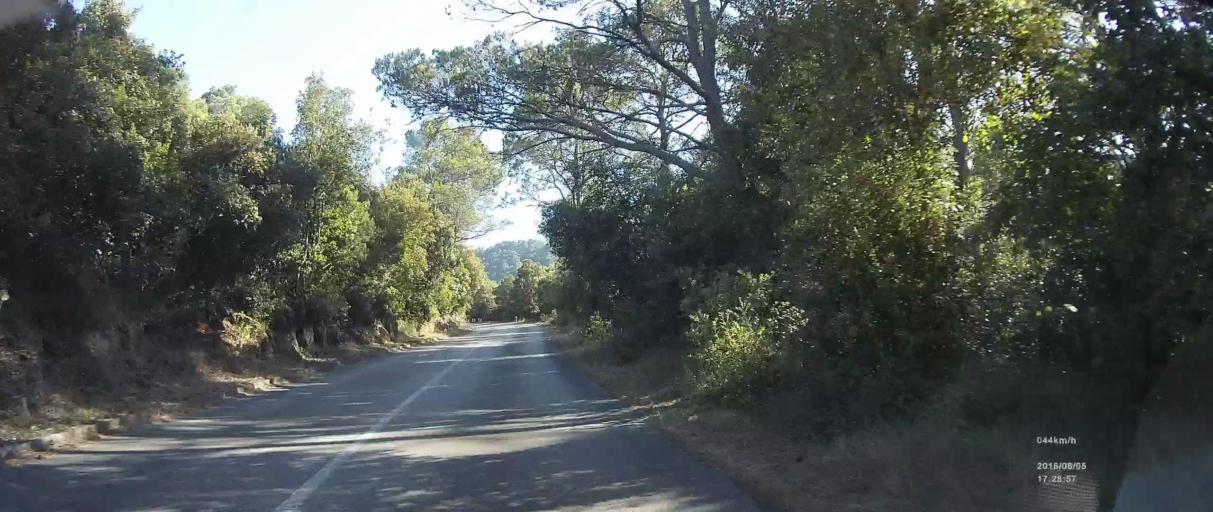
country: HR
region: Dubrovacko-Neretvanska
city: Blato
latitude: 42.7804
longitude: 17.4057
